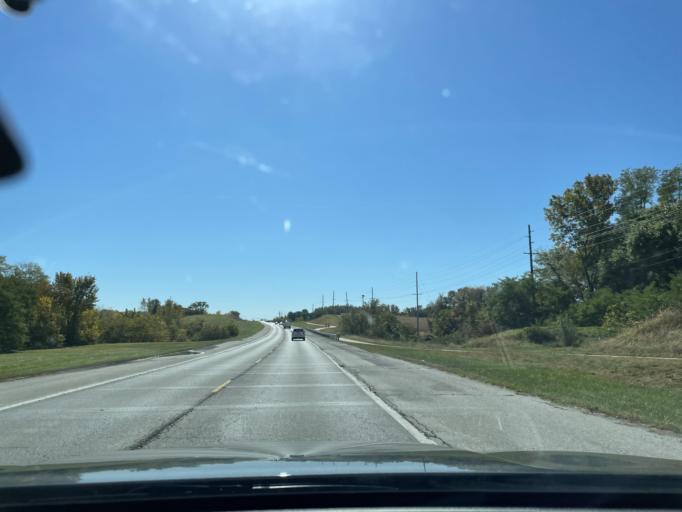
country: US
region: Missouri
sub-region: Buchanan County
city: Saint Joseph
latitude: 39.7662
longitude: -94.7688
